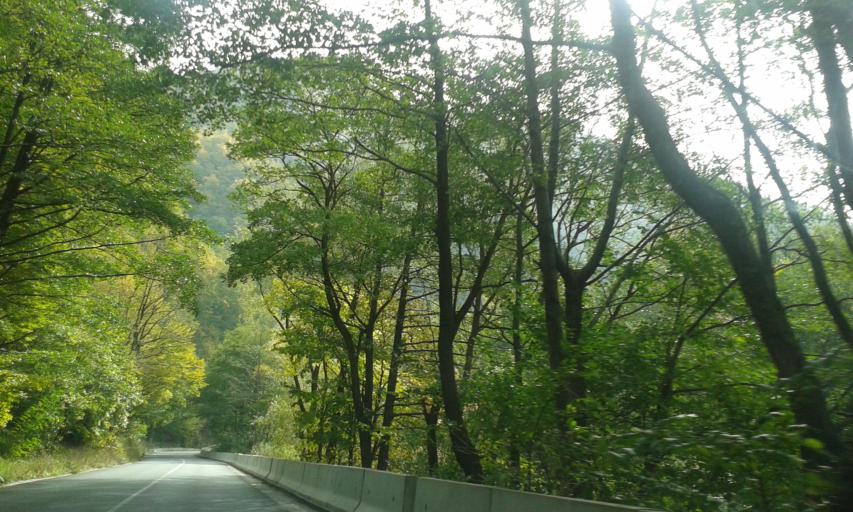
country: RO
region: Gorj
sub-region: Comuna Bumbesti-Jiu
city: Bumbesti-Jiu
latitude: 45.2404
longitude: 23.3931
